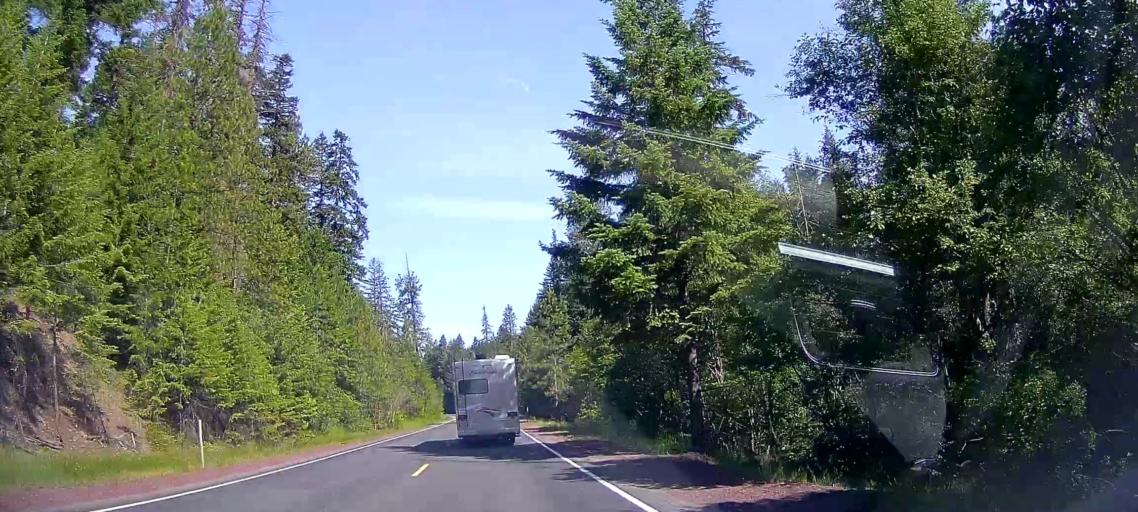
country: US
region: Oregon
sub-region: Jefferson County
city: Warm Springs
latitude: 45.0688
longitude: -121.5262
